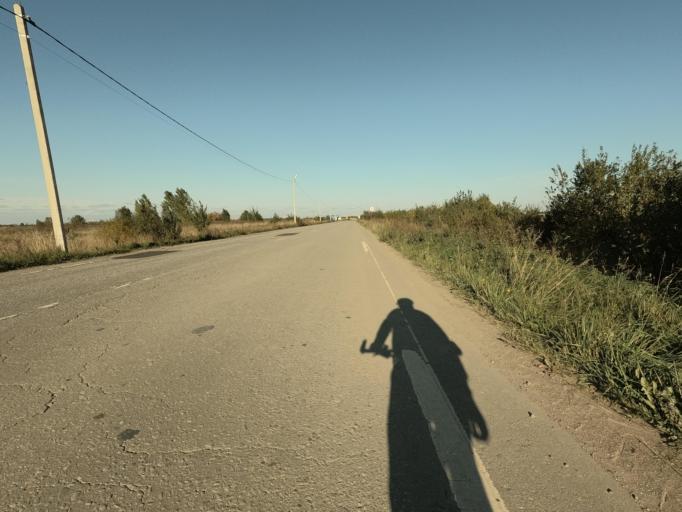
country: RU
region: St.-Petersburg
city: Petro-Slavyanka
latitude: 59.7668
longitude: 30.4892
